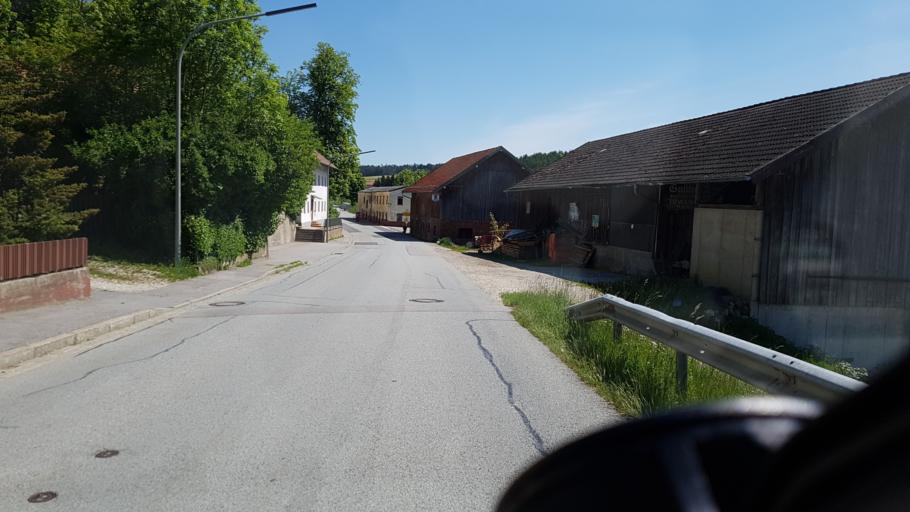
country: DE
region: Bavaria
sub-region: Lower Bavaria
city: Postmunster
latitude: 48.3677
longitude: 12.8921
